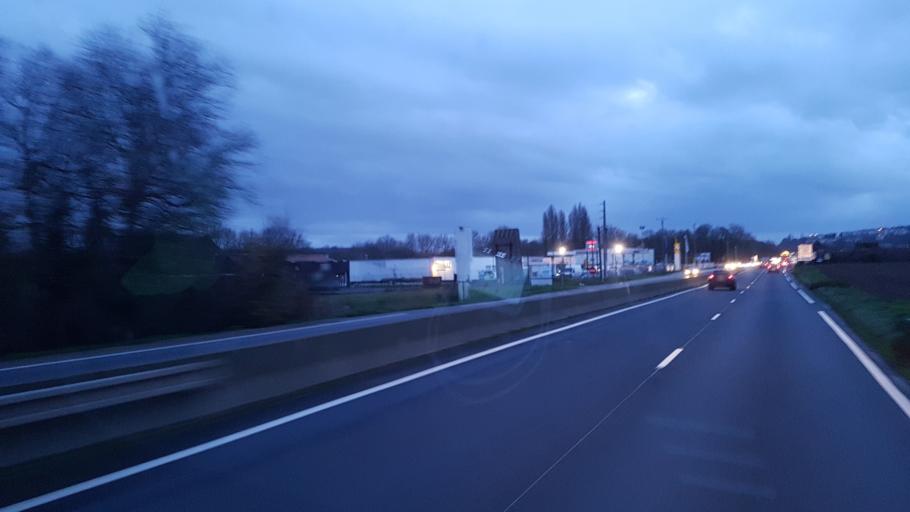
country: FR
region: Ile-de-France
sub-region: Departement de l'Essonne
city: Morigny-Champigny
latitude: 48.4631
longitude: 2.1802
